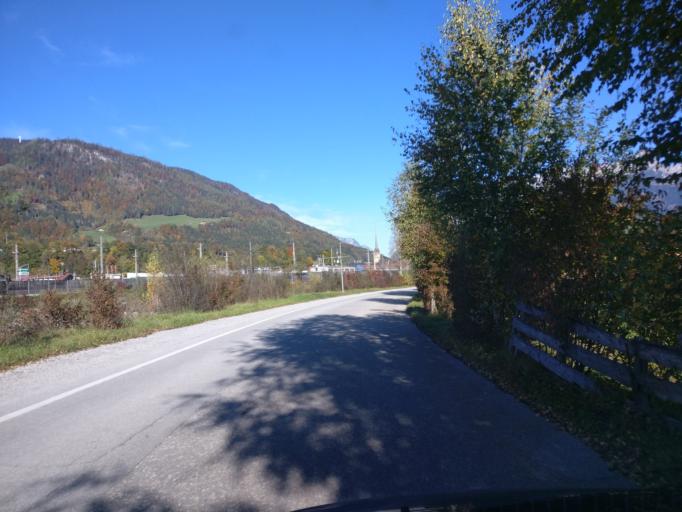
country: AT
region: Salzburg
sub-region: Politischer Bezirk Sankt Johann im Pongau
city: Bischofshofen
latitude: 47.4085
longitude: 13.2198
